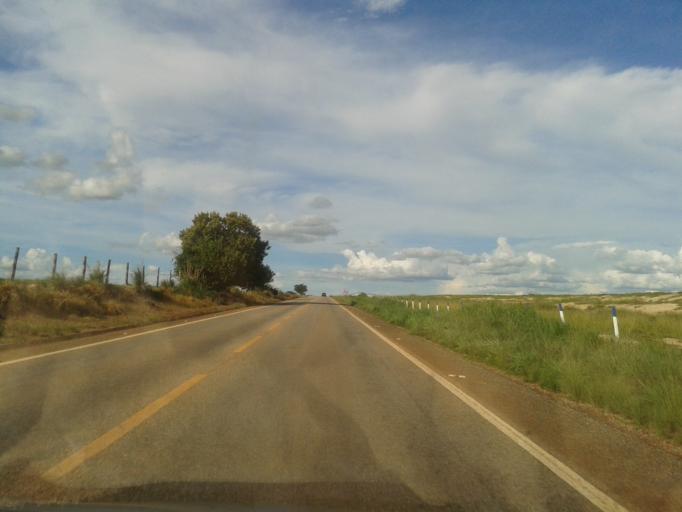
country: BR
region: Goias
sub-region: Mozarlandia
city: Mozarlandia
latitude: -14.3426
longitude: -50.4190
